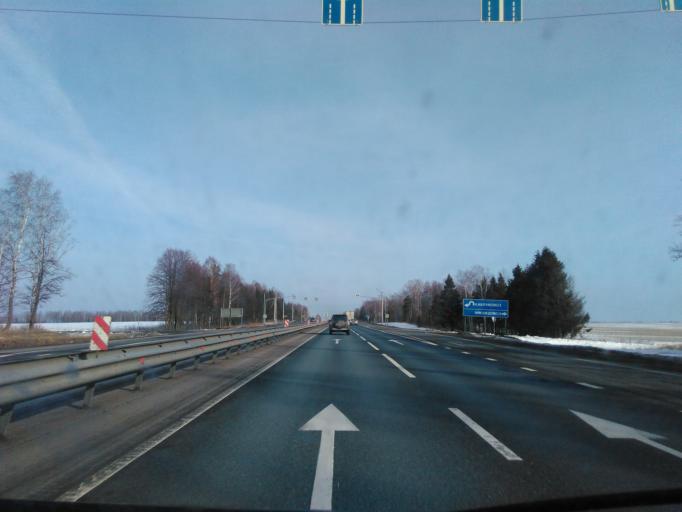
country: RU
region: Smolensk
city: Verkhnedneprovskiy
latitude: 55.1821
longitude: 33.5468
